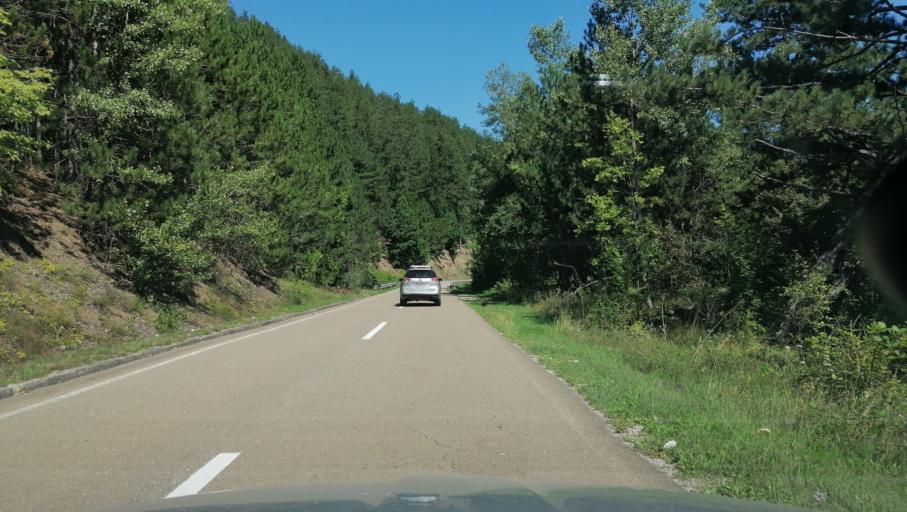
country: RS
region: Central Serbia
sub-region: Raski Okrug
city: Raska
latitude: 43.4556
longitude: 20.5863
